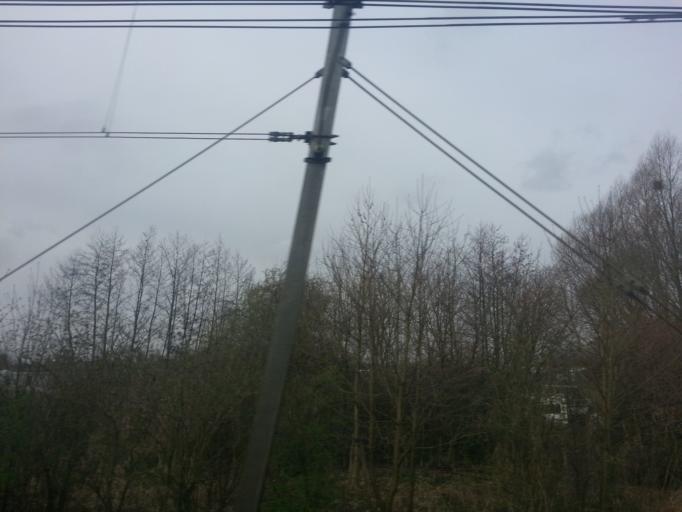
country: NL
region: Gelderland
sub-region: Gemeente Geldermalsen
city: Geldermalsen
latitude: 51.8932
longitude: 5.2670
